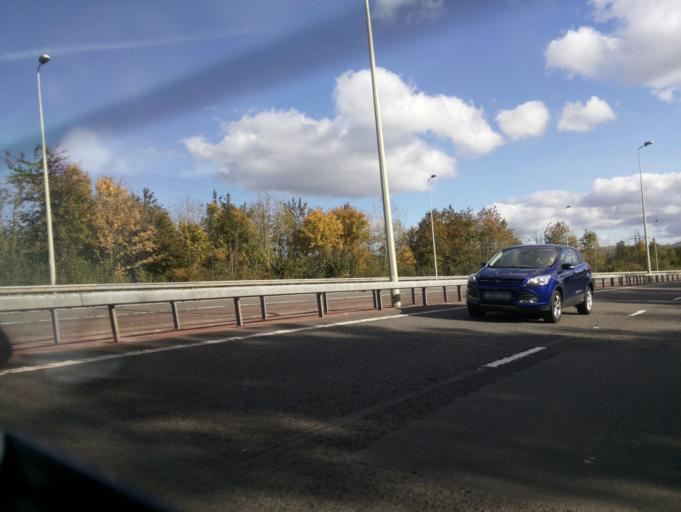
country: GB
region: Wales
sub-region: Merthyr Tydfil County Borough
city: Merthyr Tydfil
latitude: 51.7561
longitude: -3.4017
